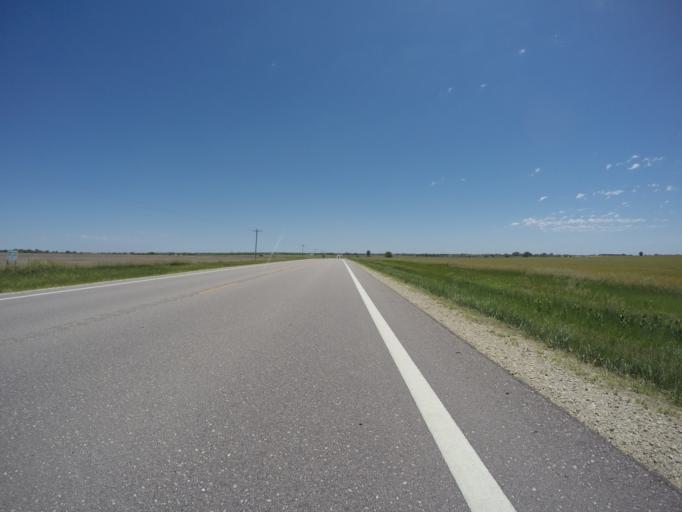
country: US
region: Kansas
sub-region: Republic County
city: Belleville
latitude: 39.8127
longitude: -97.6797
